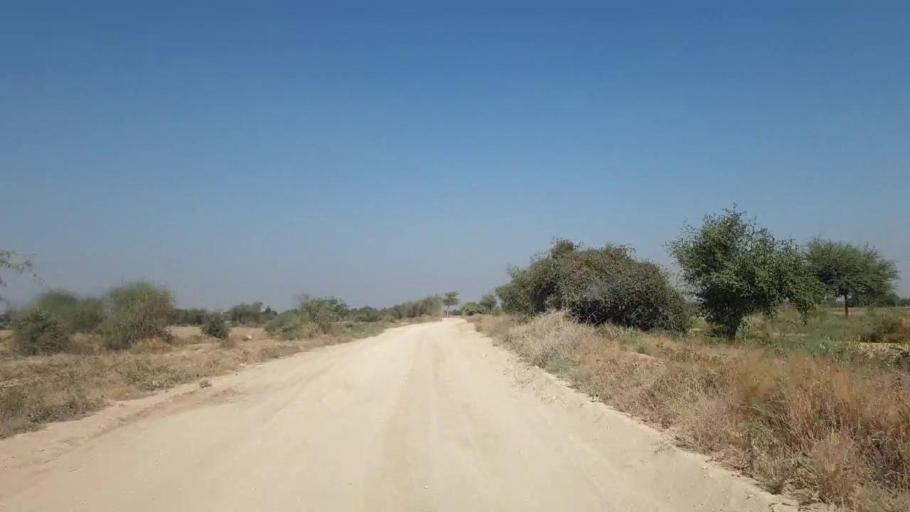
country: PK
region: Sindh
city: Jamshoro
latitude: 25.2957
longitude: 67.8141
